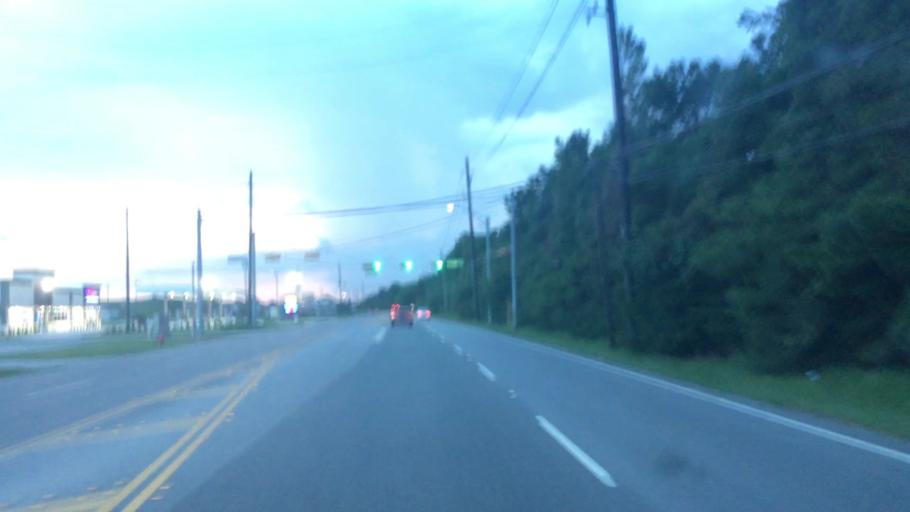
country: US
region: Texas
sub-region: Harris County
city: Humble
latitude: 29.9747
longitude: -95.2260
